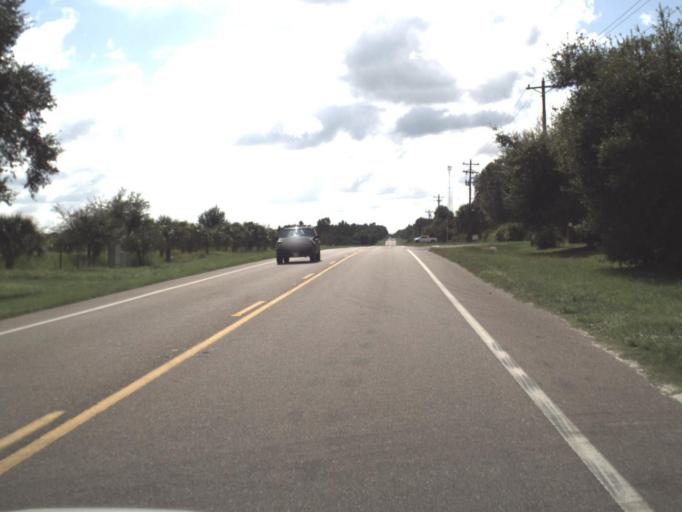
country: US
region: Florida
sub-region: Hardee County
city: Zolfo Springs
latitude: 27.4941
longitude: -81.8315
